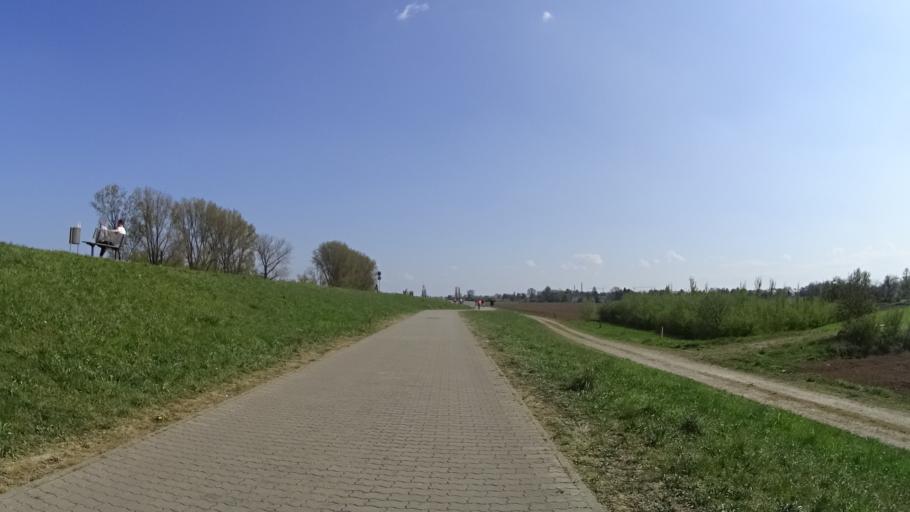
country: DE
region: North Rhine-Westphalia
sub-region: Regierungsbezirk Dusseldorf
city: Meerbusch
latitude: 51.2642
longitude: 6.7013
